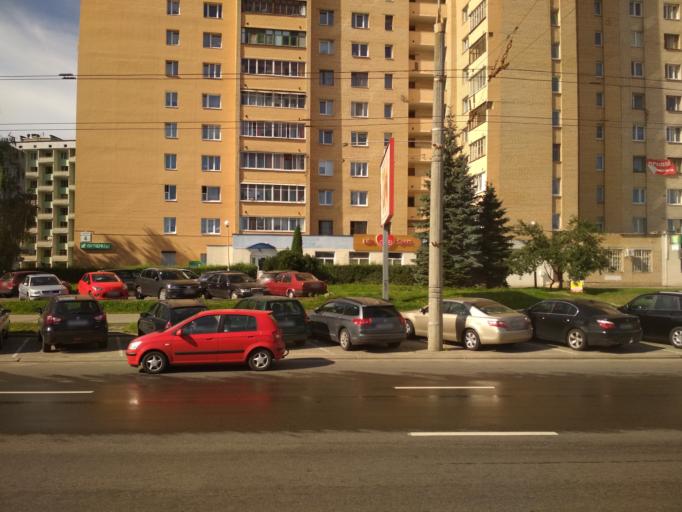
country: BY
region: Minsk
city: Minsk
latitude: 53.8895
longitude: 27.5439
